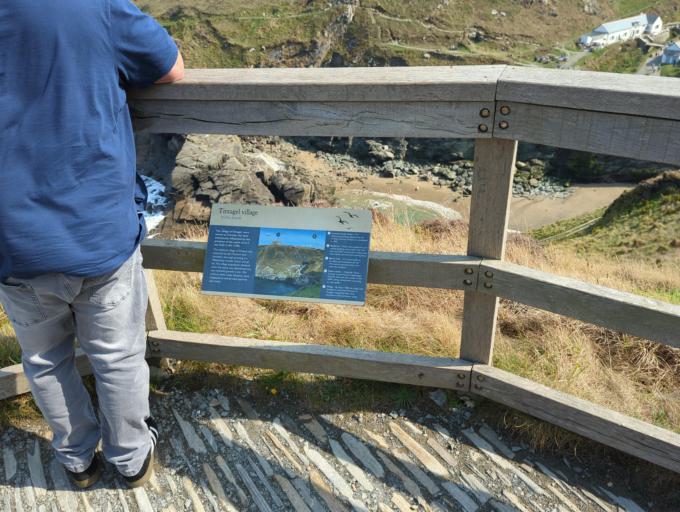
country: GB
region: England
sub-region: Cornwall
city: Tintagel
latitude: 50.6691
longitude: -4.7605
